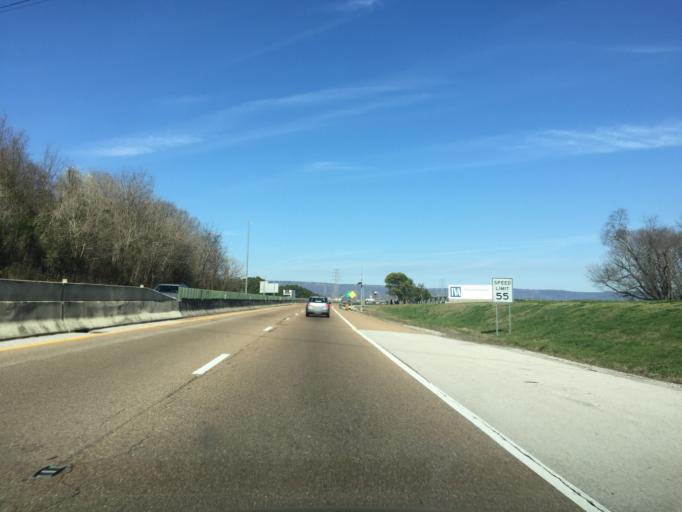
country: US
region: Tennessee
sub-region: Hamilton County
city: East Chattanooga
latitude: 35.0937
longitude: -85.2241
